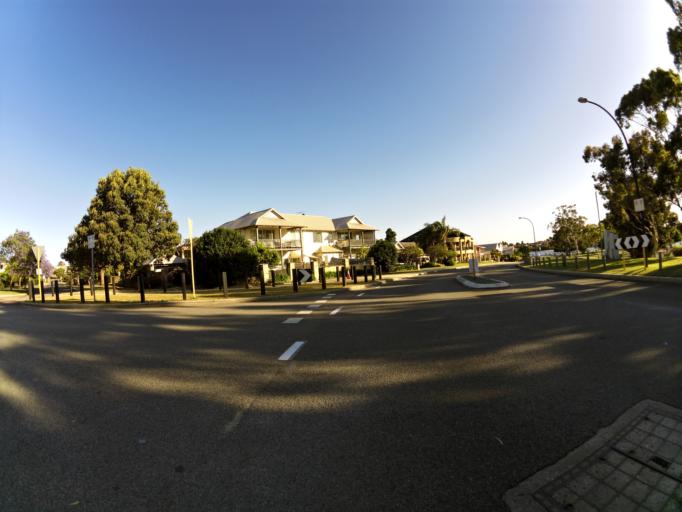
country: AU
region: Western Australia
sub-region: Melville
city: Mount Pleasant
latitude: -32.0247
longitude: 115.8525
